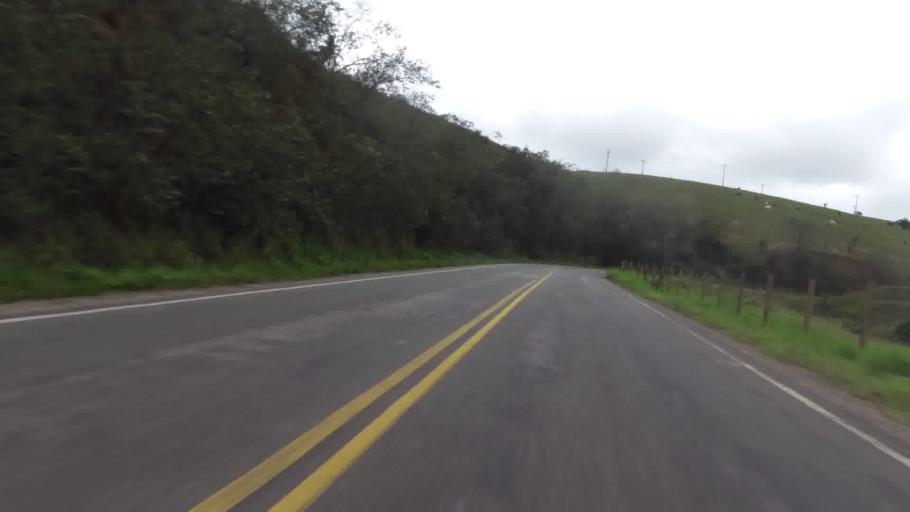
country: BR
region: Espirito Santo
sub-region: Alfredo Chaves
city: Alfredo Chaves
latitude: -20.6684
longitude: -40.7067
